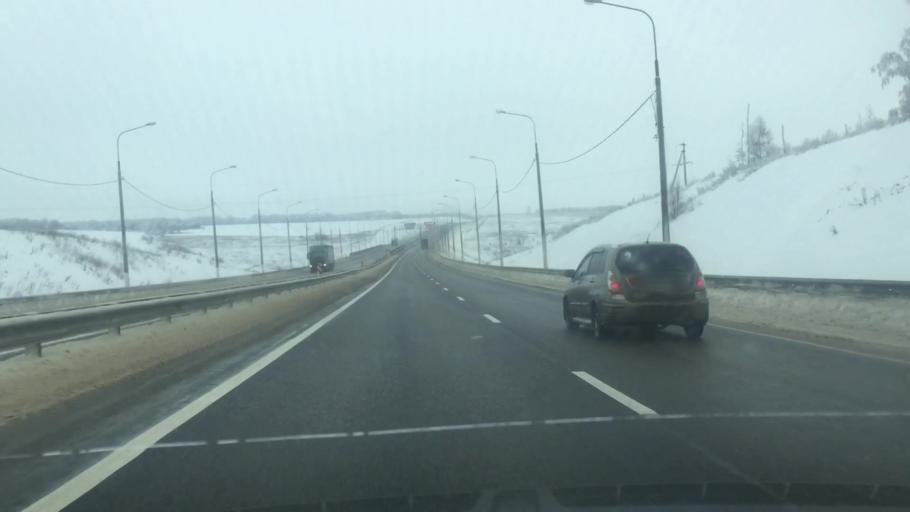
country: RU
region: Lipetsk
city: Stanovoye
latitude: 52.8677
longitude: 38.2836
